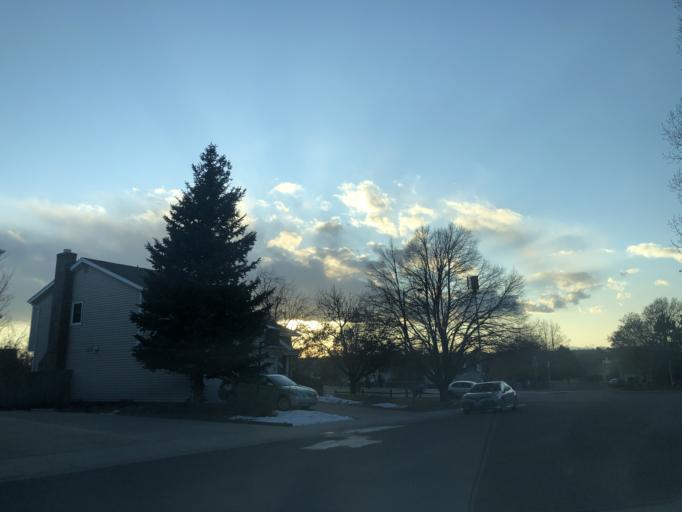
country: US
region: Colorado
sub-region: Adams County
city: Aurora
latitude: 39.7042
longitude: -104.8011
